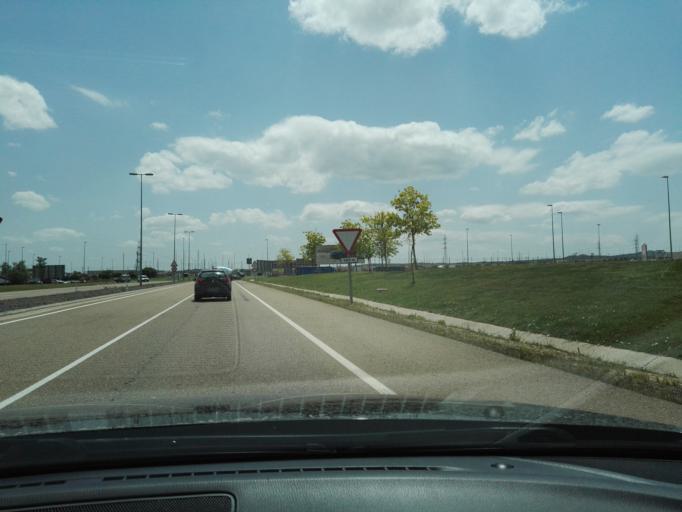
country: ES
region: Aragon
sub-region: Provincia de Zaragoza
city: Montecanal
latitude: 41.6414
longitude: -0.9934
